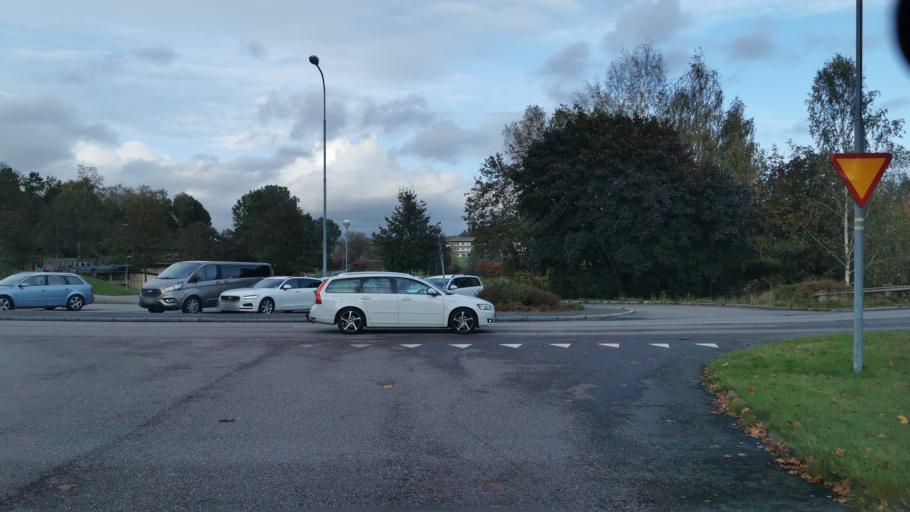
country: SE
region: Vaestra Goetaland
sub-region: Partille Kommun
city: Partille
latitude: 57.7161
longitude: 12.0730
